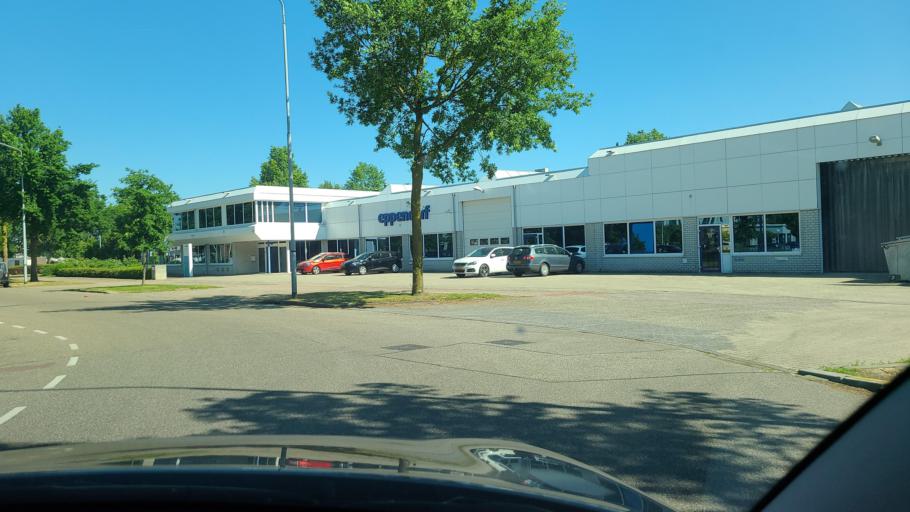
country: NL
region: Gelderland
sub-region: Gemeente Nijmegen
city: Lindenholt
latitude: 51.8269
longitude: 5.7893
